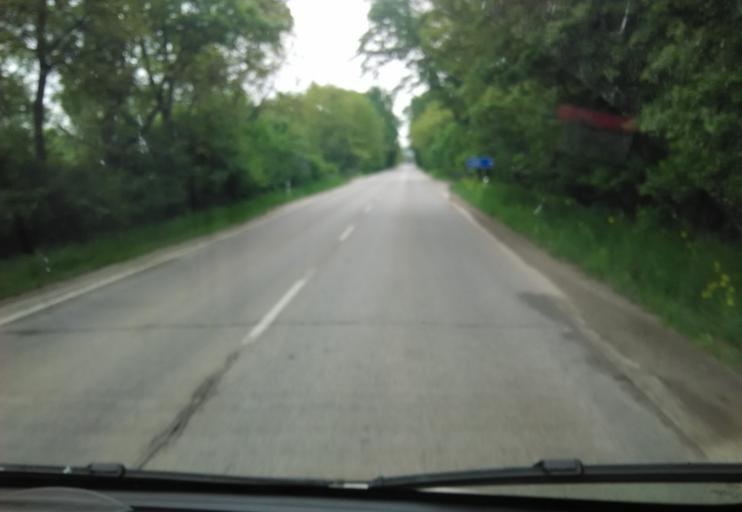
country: SK
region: Trnavsky
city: Leopoldov
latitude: 48.4605
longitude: 17.7438
